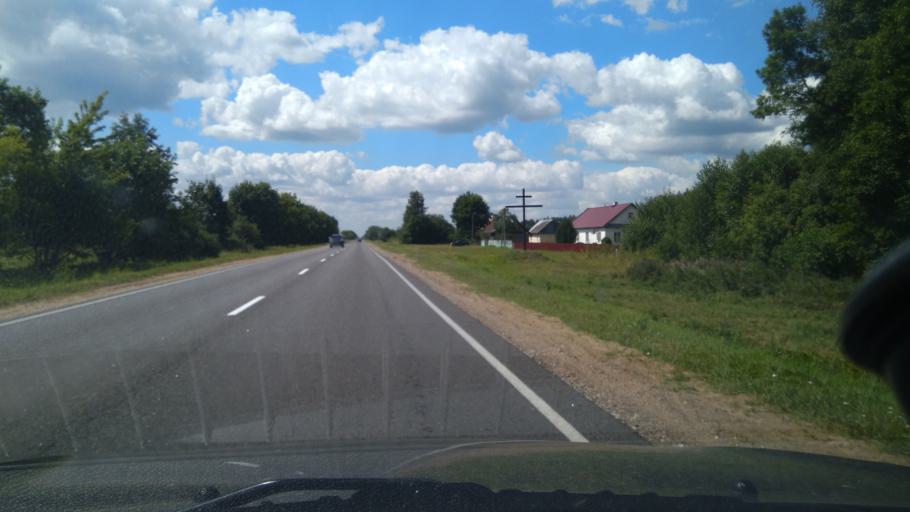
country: BY
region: Brest
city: Nyakhachava
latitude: 52.6550
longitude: 25.2277
